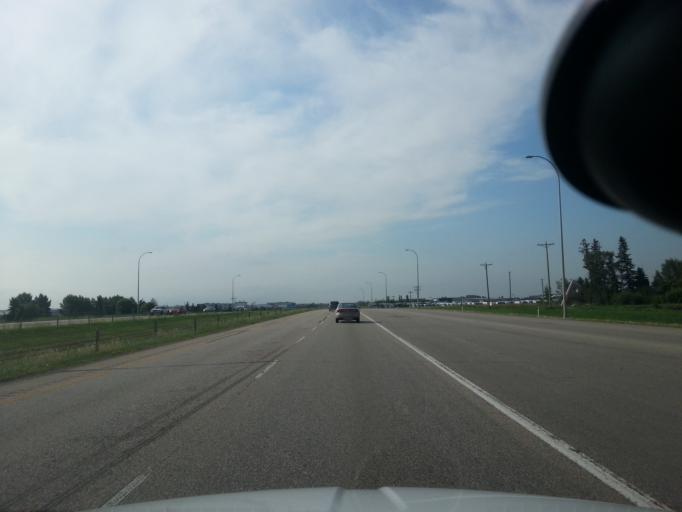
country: CA
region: Alberta
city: Red Deer
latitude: 52.3124
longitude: -113.8614
